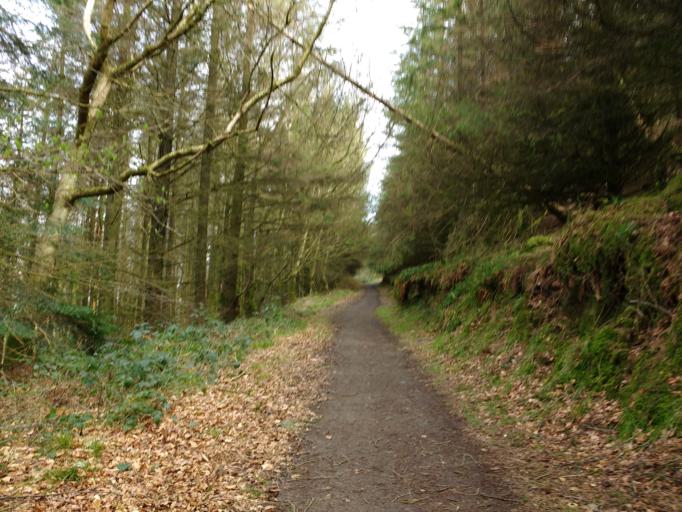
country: IE
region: Leinster
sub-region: Kilkenny
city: Callan
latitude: 52.6644
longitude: -7.5308
